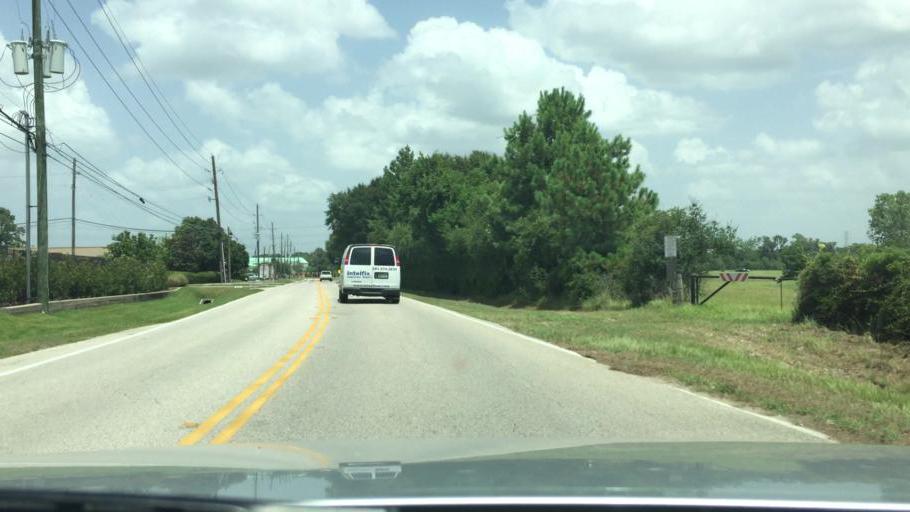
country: US
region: Texas
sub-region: Harris County
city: Hudson
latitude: 29.9403
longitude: -95.5159
